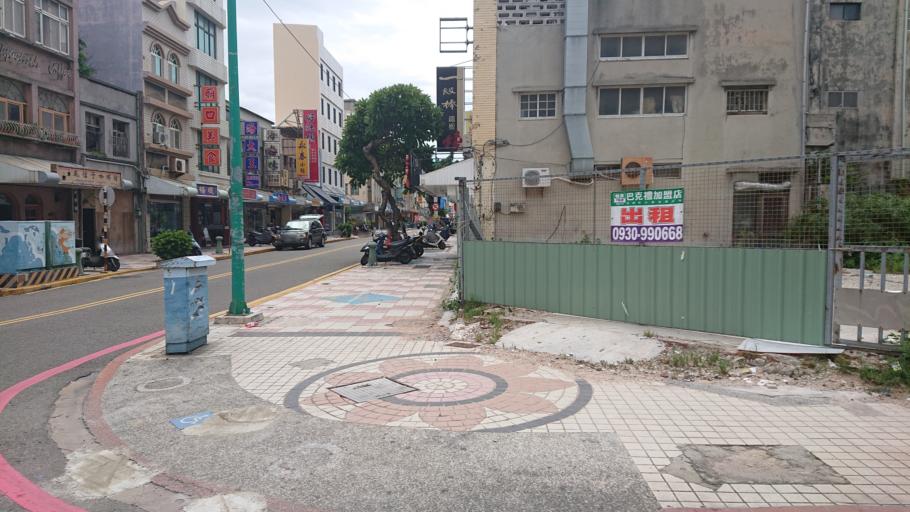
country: TW
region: Taiwan
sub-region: Penghu
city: Ma-kung
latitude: 23.5652
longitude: 119.5676
